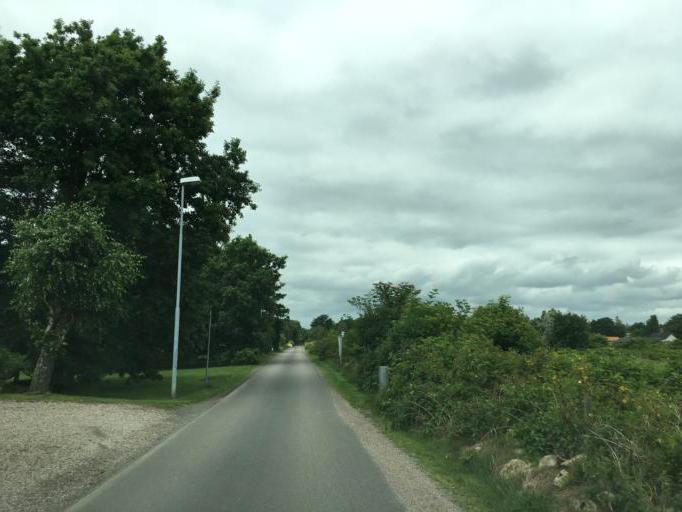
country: SE
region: Skane
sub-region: Angelholms Kommun
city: Vejbystrand
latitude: 56.3248
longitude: 12.7617
